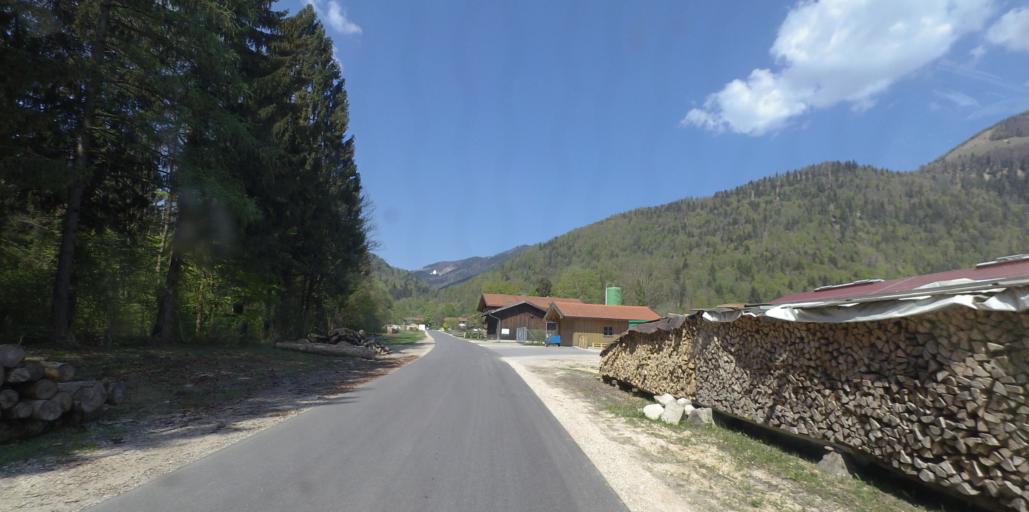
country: DE
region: Bavaria
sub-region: Upper Bavaria
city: Schleching
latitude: 47.7267
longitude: 12.4041
